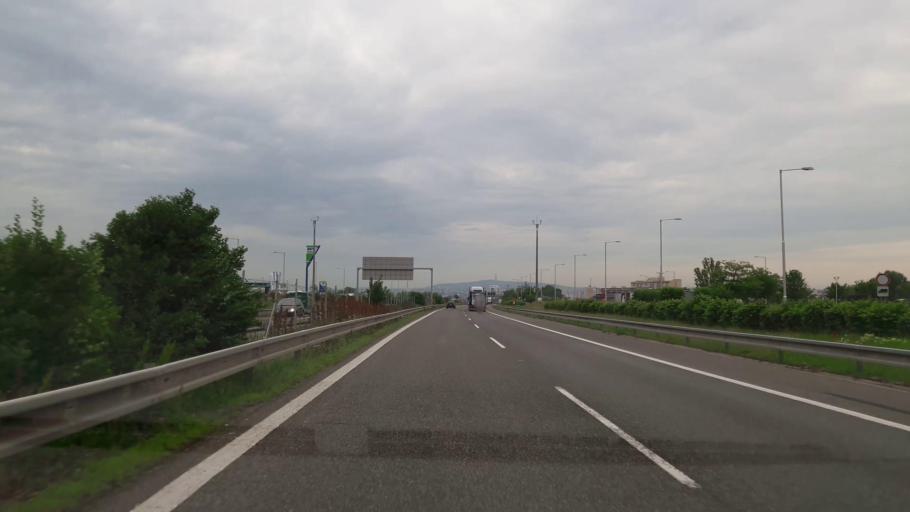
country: AT
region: Burgenland
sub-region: Politischer Bezirk Neusiedl am See
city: Kittsee
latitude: 48.0862
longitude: 17.0991
